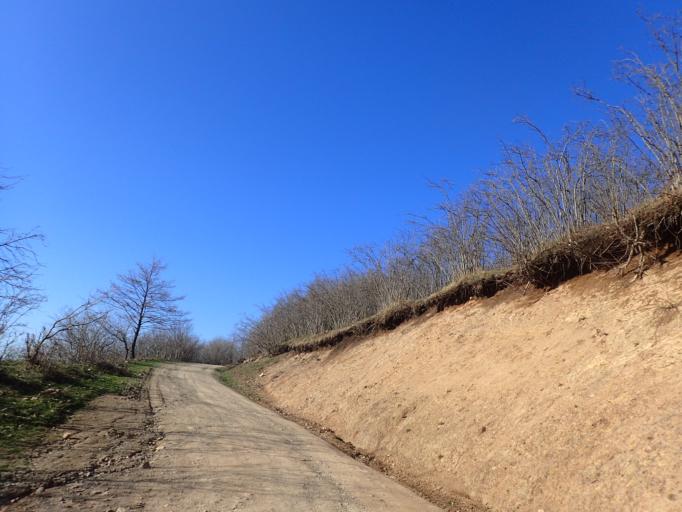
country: TR
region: Ordu
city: Camas
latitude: 40.8601
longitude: 37.5009
